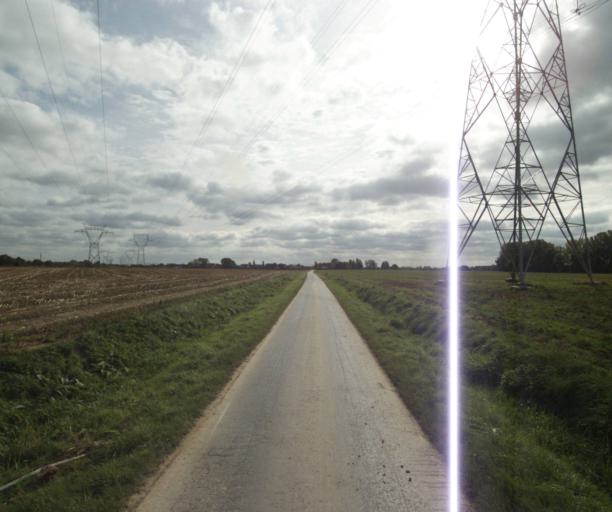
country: FR
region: Nord-Pas-de-Calais
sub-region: Departement du Nord
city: Bois-Grenier
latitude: 50.6588
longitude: 2.8615
